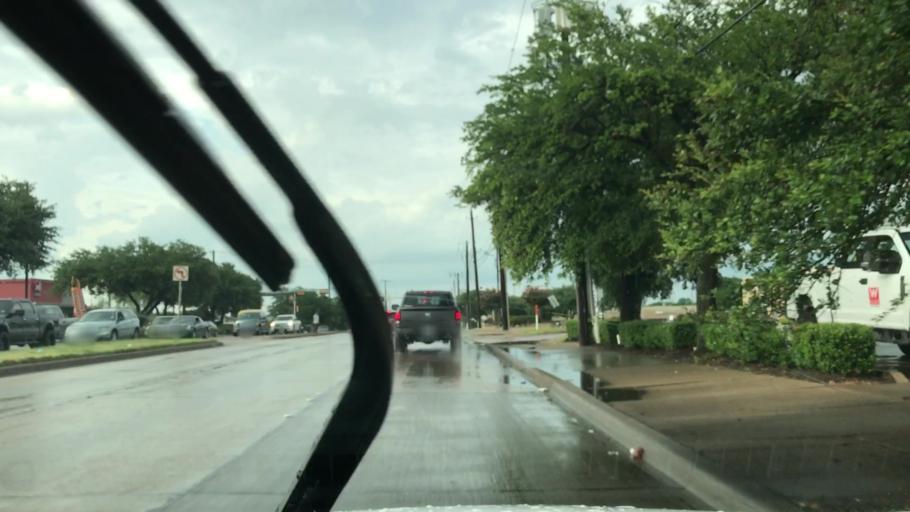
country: US
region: Texas
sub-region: Dallas County
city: Garland
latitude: 32.8580
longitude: -96.6462
